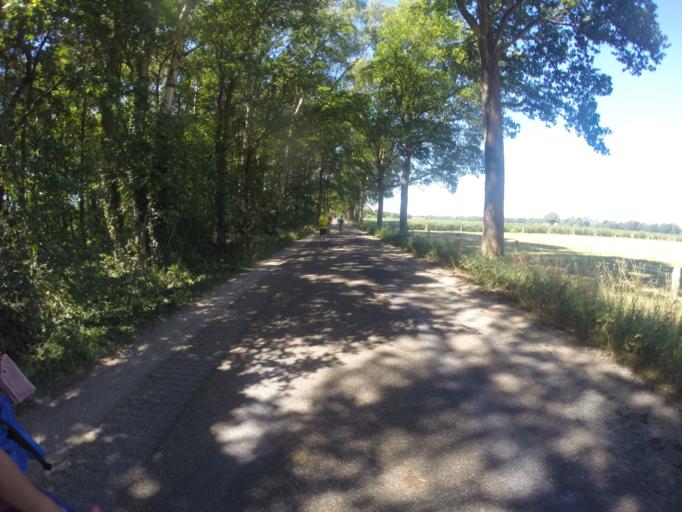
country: NL
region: Gelderland
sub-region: Gemeente Lochem
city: Lochem
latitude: 52.1369
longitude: 6.4171
